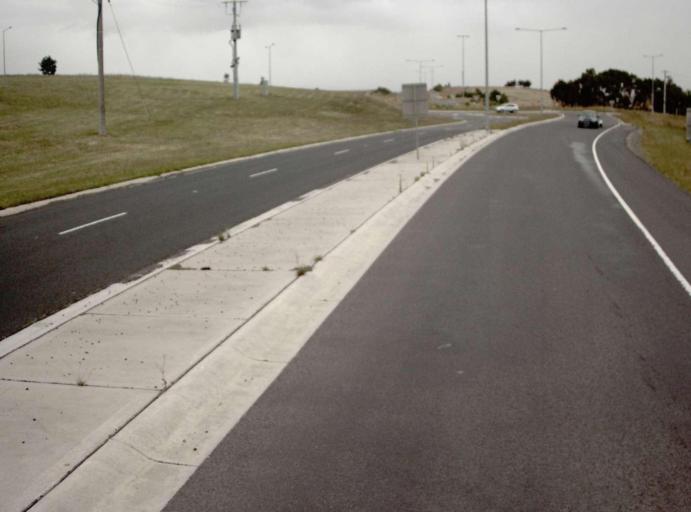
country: AU
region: Victoria
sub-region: Yarra Ranges
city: Yarra Glen
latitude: -37.6447
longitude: 145.3979
